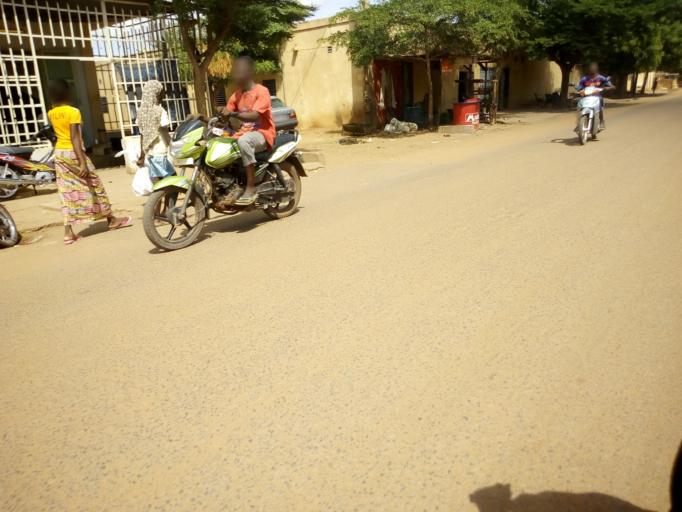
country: ML
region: Segou
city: Segou
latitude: 13.4334
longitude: -6.2639
